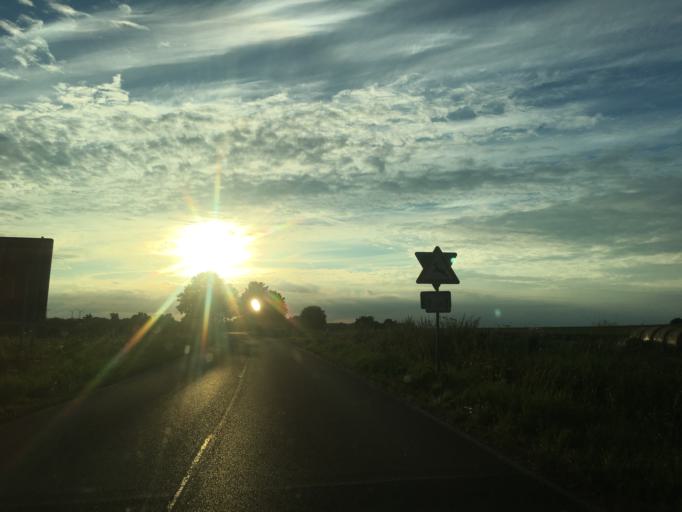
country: DE
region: North Rhine-Westphalia
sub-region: Regierungsbezirk Koln
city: Linnich
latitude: 50.9849
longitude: 6.2987
